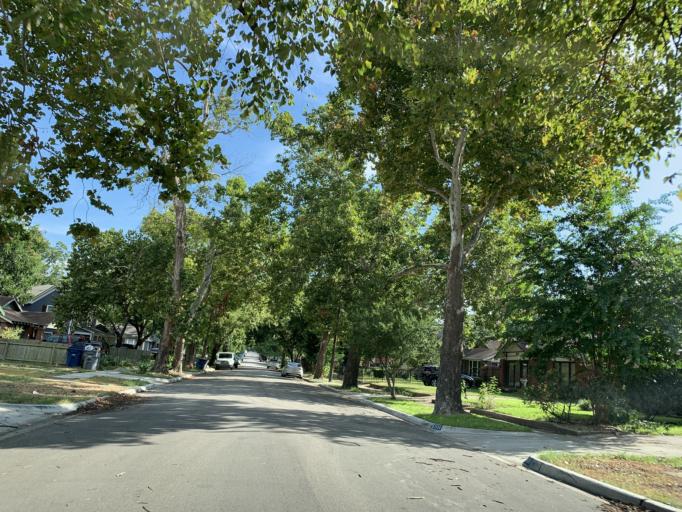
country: US
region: Texas
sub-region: Dallas County
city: Cockrell Hill
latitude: 32.7345
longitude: -96.8542
